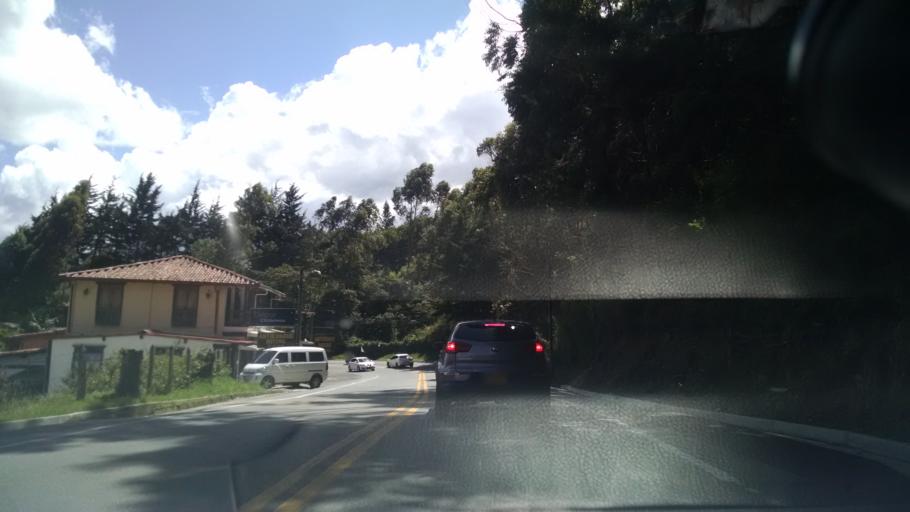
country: CO
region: Antioquia
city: El Retiro
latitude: 6.1233
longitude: -75.5013
